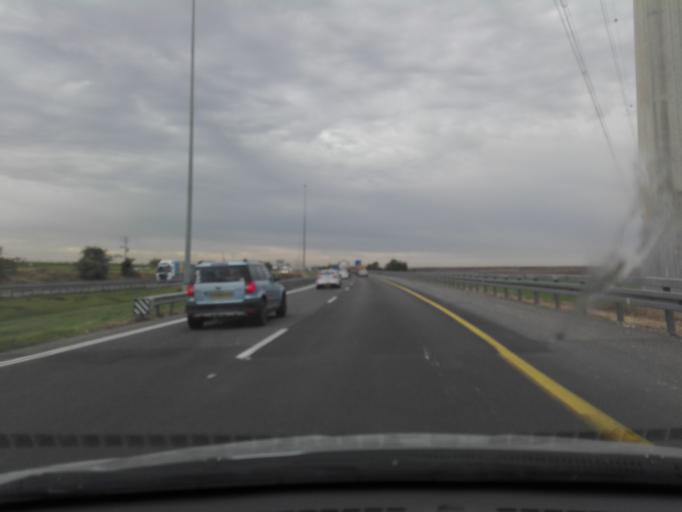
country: IL
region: Central District
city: Ramla
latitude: 31.8988
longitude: 34.8836
